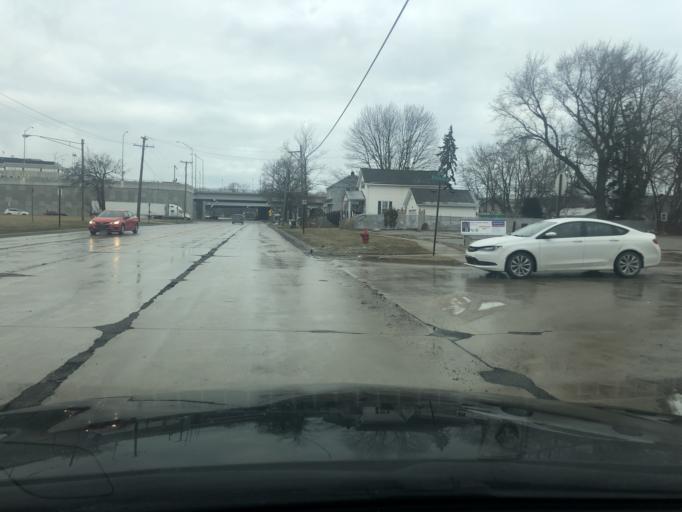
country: US
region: Michigan
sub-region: Saint Clair County
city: Port Huron
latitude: 42.9967
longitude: -82.4344
